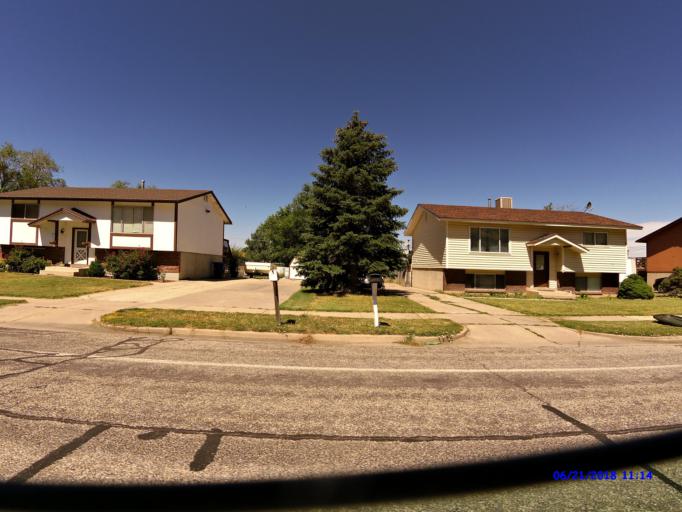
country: US
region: Utah
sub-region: Weber County
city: North Ogden
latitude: 41.2807
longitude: -111.9593
